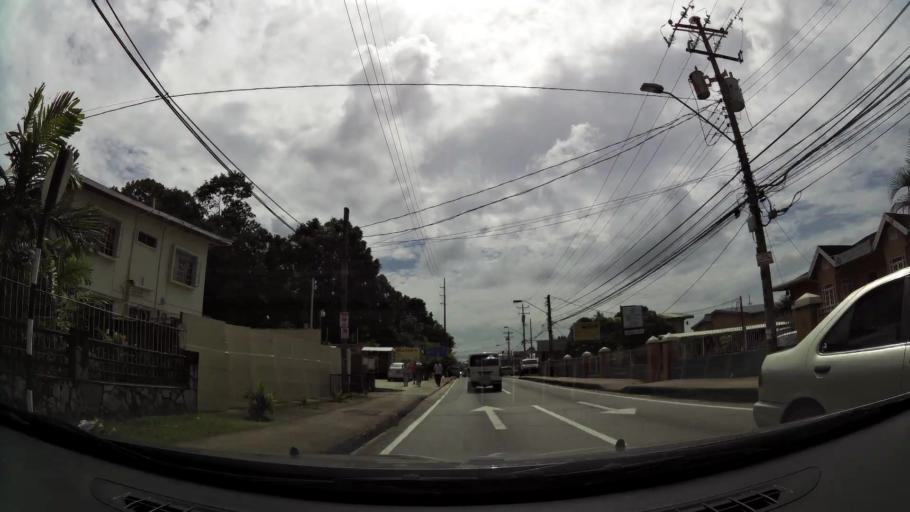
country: TT
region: Diego Martin
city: Petit Valley
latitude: 10.6888
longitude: -61.5541
